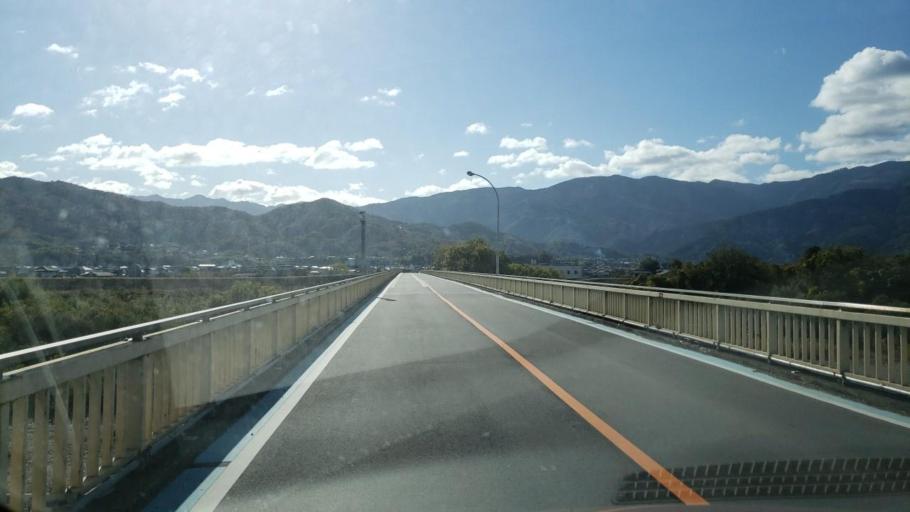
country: JP
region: Tokushima
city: Wakimachi
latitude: 34.0693
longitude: 134.2372
